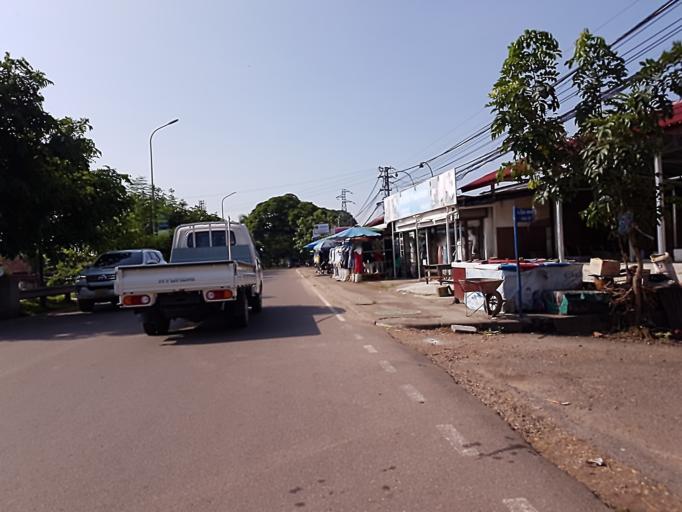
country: LA
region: Vientiane
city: Vientiane
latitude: 17.9501
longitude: 102.6229
